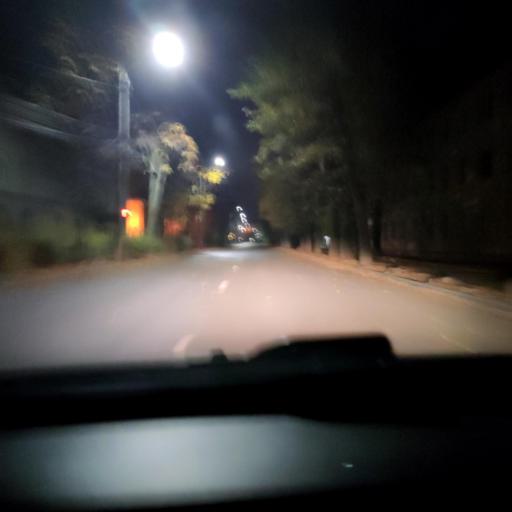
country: RU
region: Voronezj
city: Voronezh
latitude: 51.6860
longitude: 39.1783
